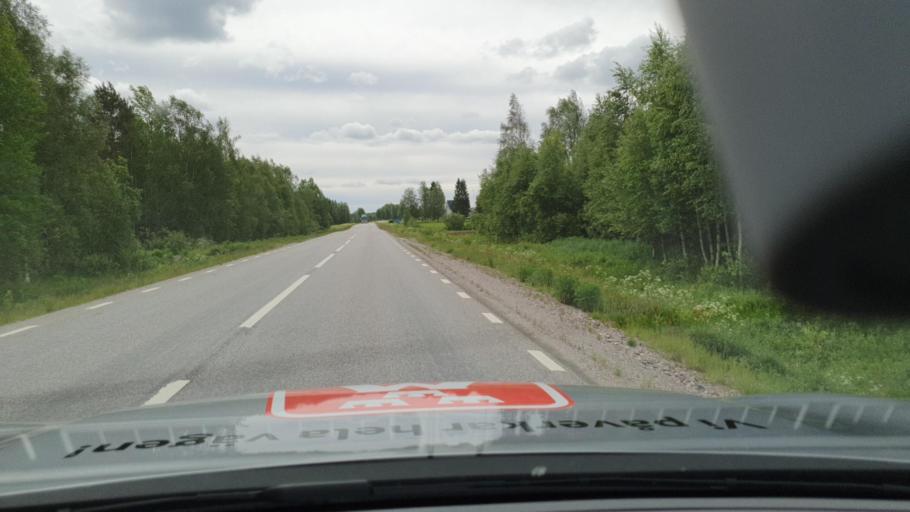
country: SE
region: Norrbotten
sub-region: Kalix Kommun
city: Kalix
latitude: 65.9776
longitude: 23.4602
